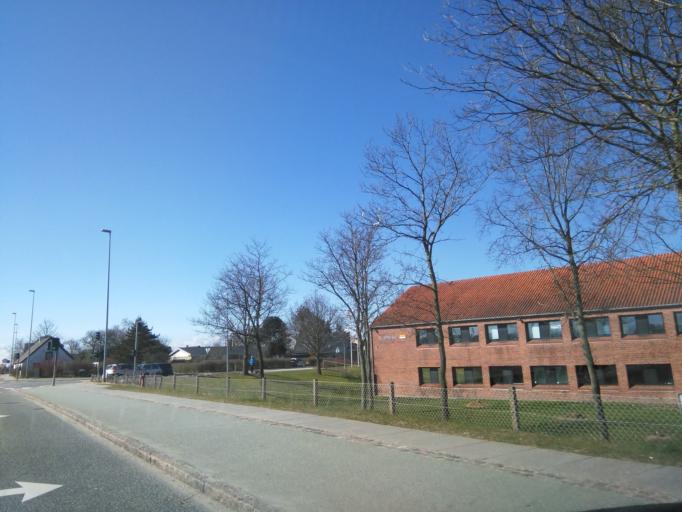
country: DK
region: Central Jutland
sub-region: Arhus Kommune
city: Tranbjerg
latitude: 56.1049
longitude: 10.1459
